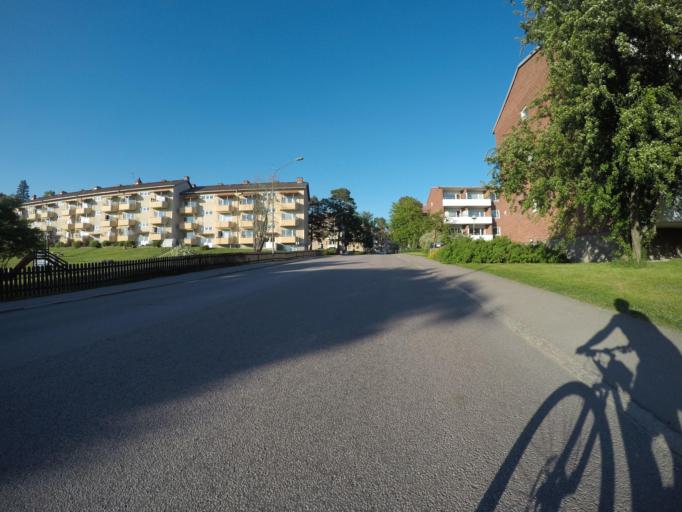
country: SE
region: Vaestmanland
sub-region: Vasteras
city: Vasteras
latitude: 59.6137
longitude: 16.5800
